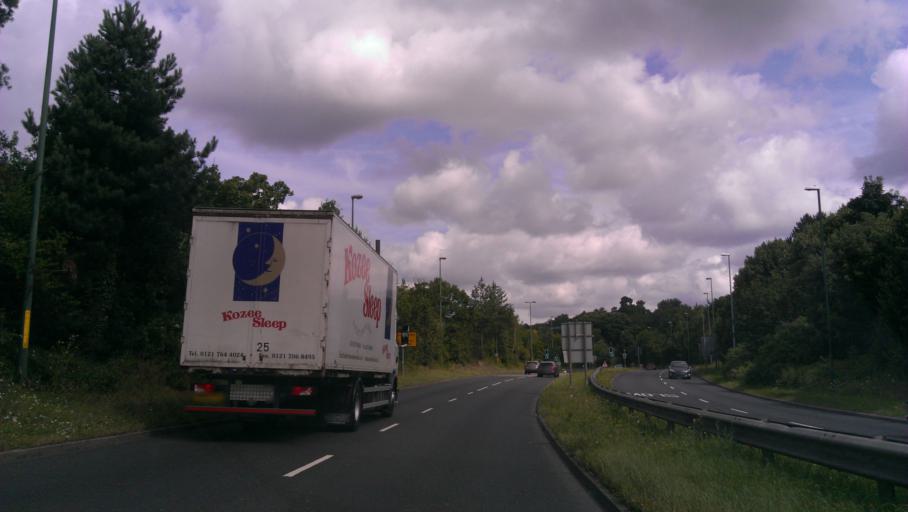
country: GB
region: England
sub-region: Kent
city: Maidstone
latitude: 51.2888
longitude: 0.5175
